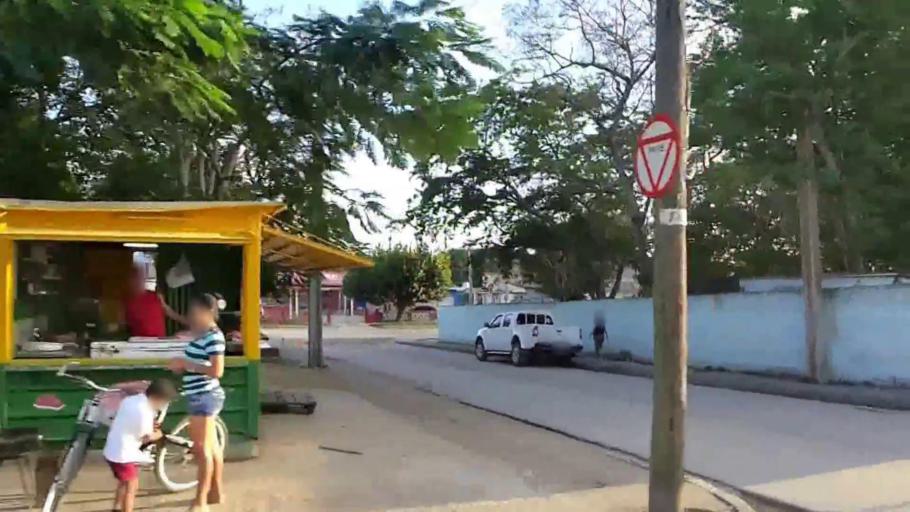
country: CU
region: Camaguey
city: Camaguey
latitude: 21.3950
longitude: -77.9048
